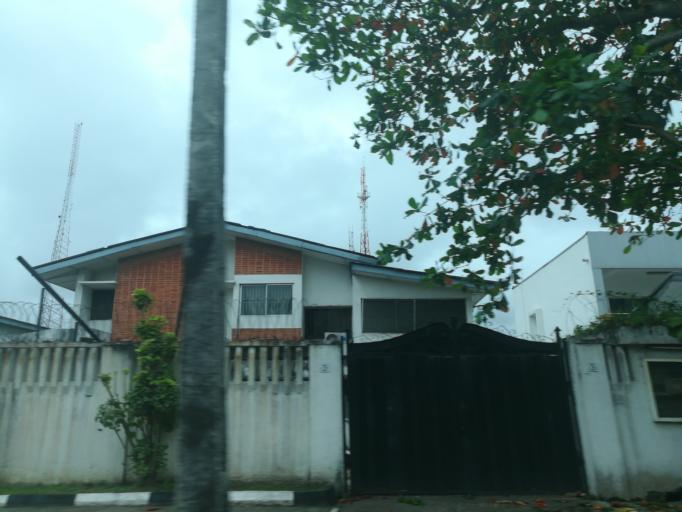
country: NG
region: Lagos
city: Ikoyi
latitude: 6.4261
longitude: 3.4214
